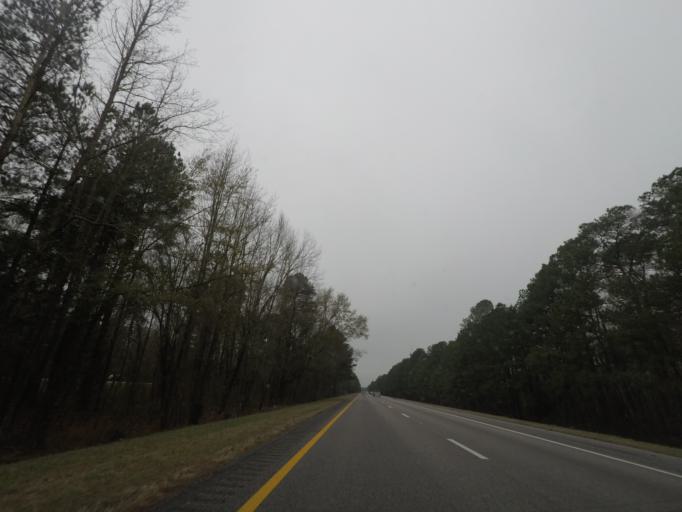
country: US
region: South Carolina
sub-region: Sumter County
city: East Sumter
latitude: 33.9245
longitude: -80.0754
